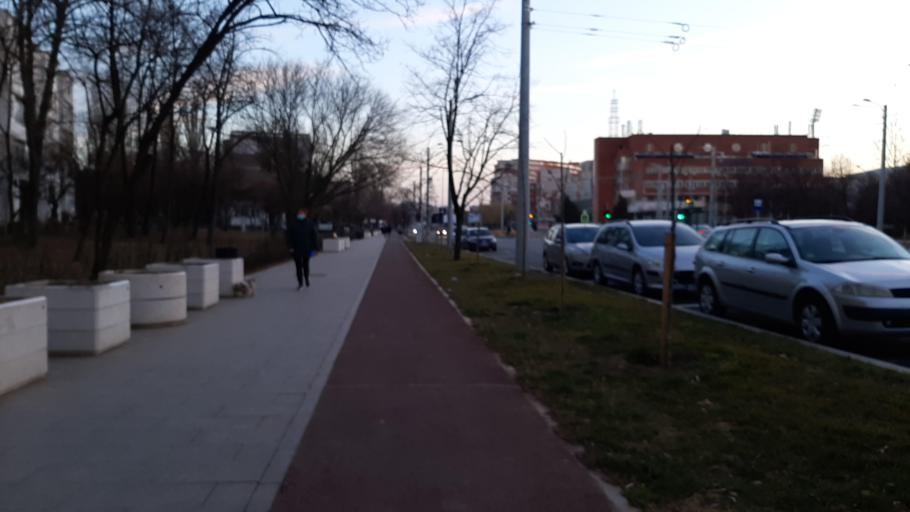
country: RO
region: Galati
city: Galati
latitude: 45.4316
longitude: 28.0254
